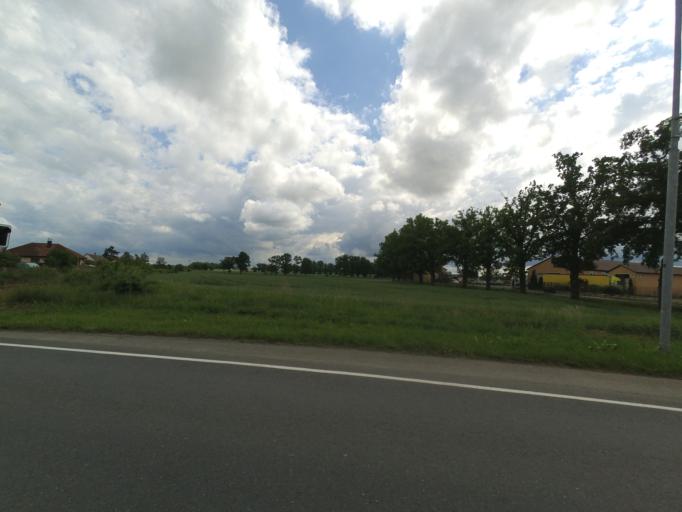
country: CZ
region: Plzensky
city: Bor
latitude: 49.7084
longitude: 12.7845
